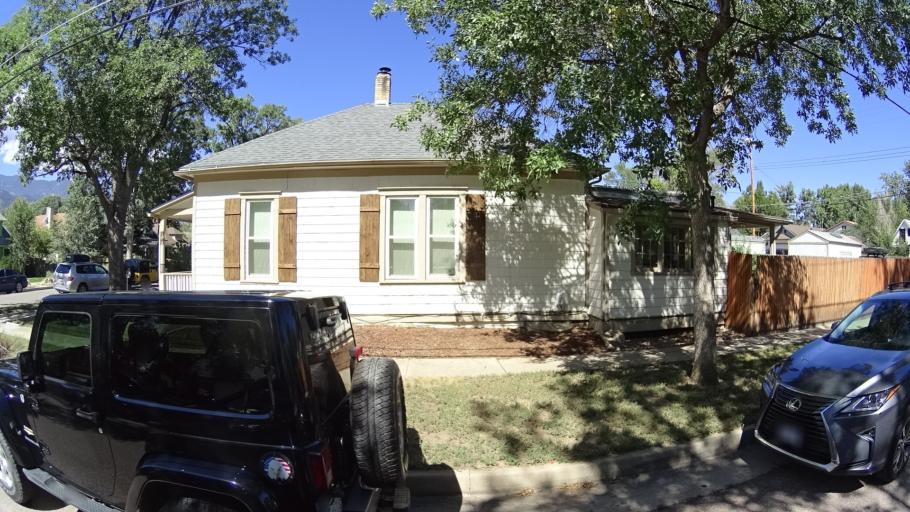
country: US
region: Colorado
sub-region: El Paso County
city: Colorado Springs
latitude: 38.8460
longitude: -104.8566
